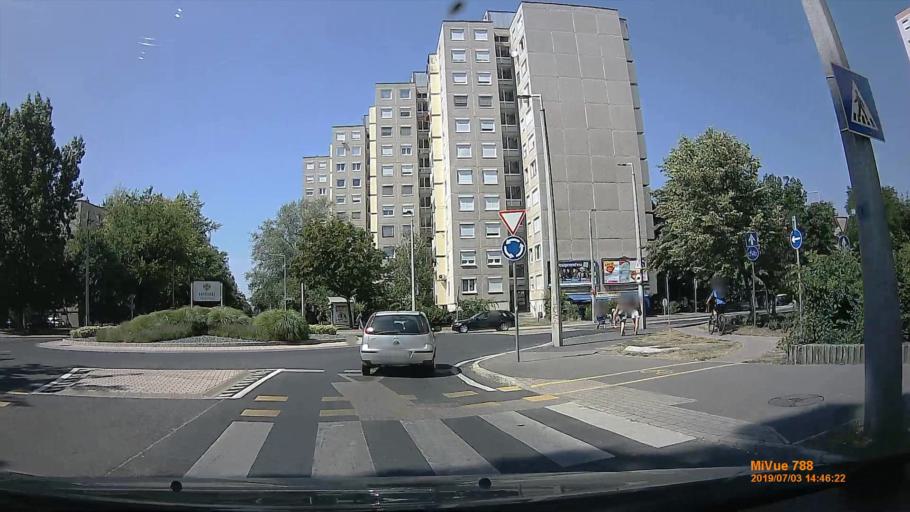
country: HU
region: Gyor-Moson-Sopron
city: Gyor
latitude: 47.6742
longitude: 17.6495
